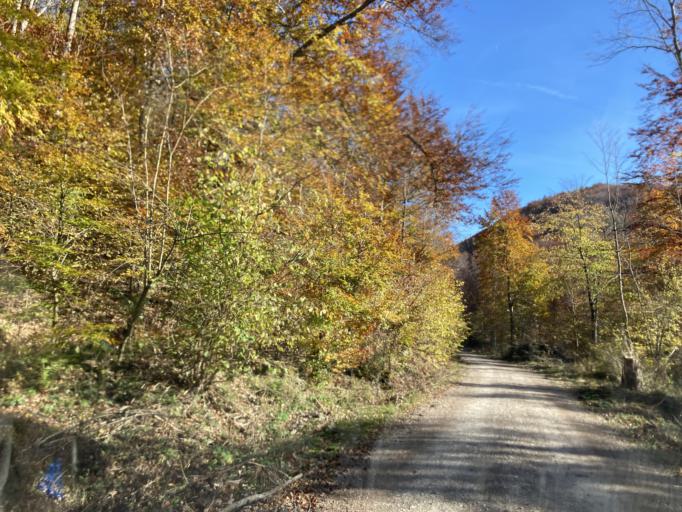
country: DE
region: Baden-Wuerttemberg
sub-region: Tuebingen Region
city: Gomaringen
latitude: 48.4110
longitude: 9.1440
